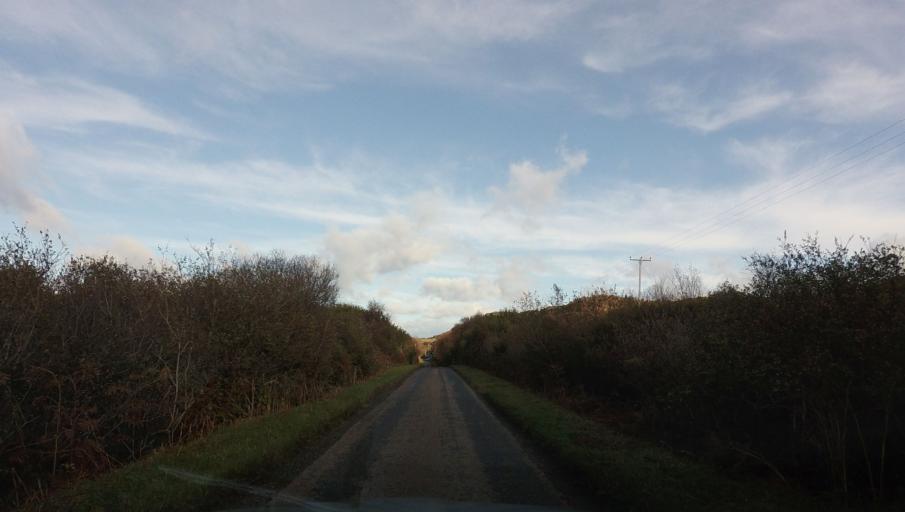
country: GB
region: Scotland
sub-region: Argyll and Bute
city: Isle Of Mull
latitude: 56.3326
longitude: -6.1769
